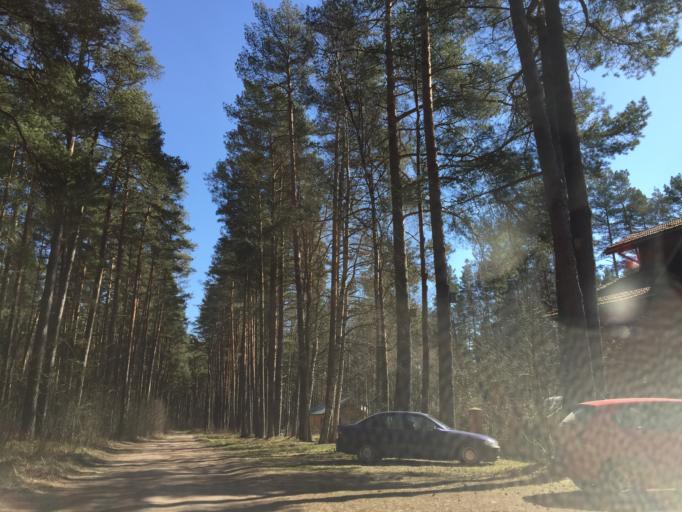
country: LV
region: Jurmala
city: Jurmala
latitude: 56.9458
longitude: 23.7062
